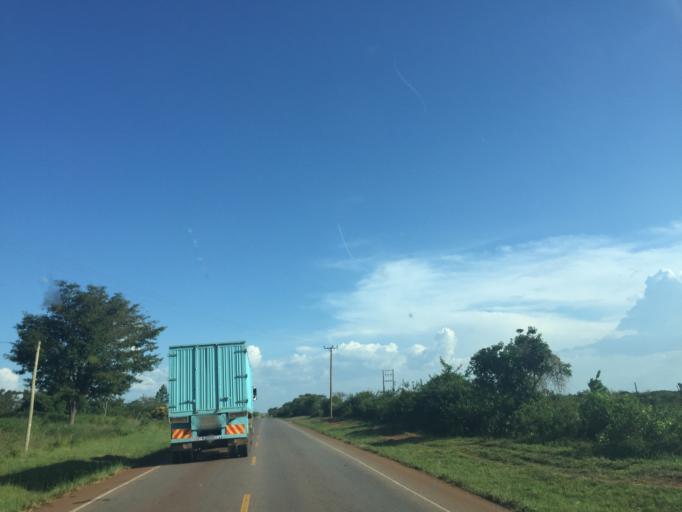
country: UG
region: Central Region
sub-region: Nakasongola District
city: Nakasongola
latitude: 1.2919
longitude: 32.4268
